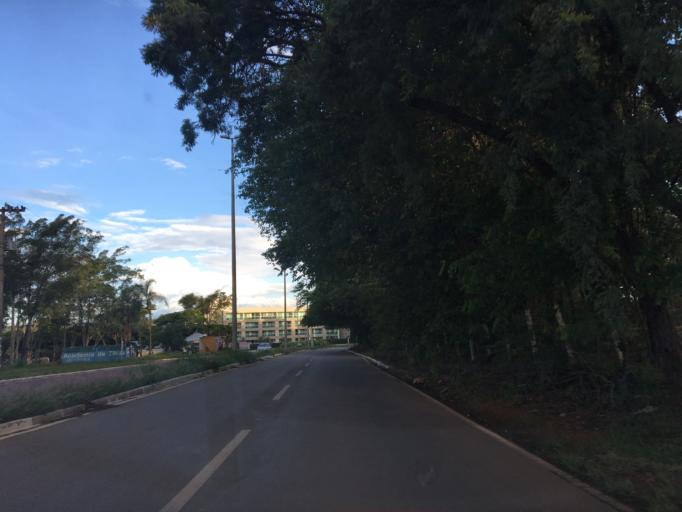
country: BR
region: Federal District
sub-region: Brasilia
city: Brasilia
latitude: -15.8055
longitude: -47.8327
